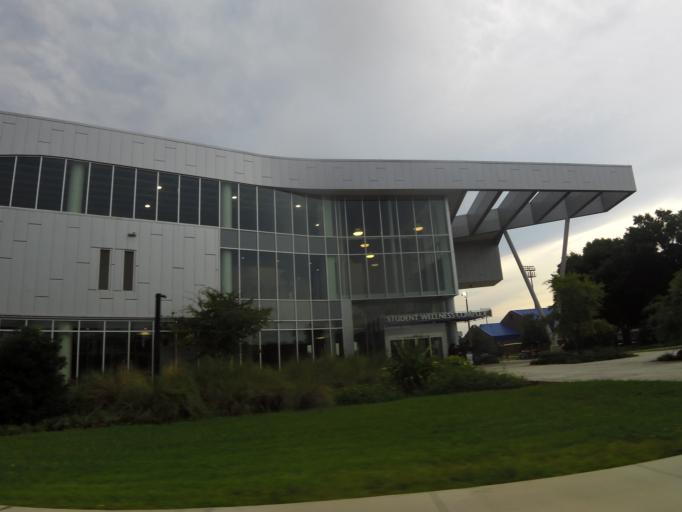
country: US
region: Florida
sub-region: Duval County
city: Jacksonville Beach
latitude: 30.2730
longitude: -81.5095
